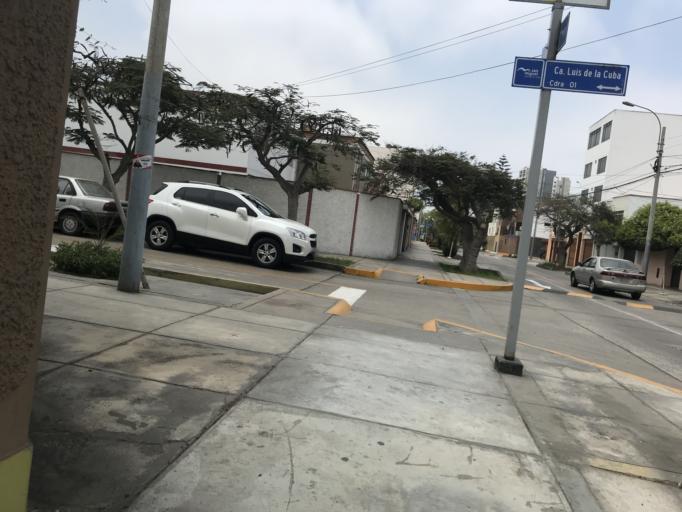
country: PE
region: Callao
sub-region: Callao
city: Callao
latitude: -12.0801
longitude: -77.0805
